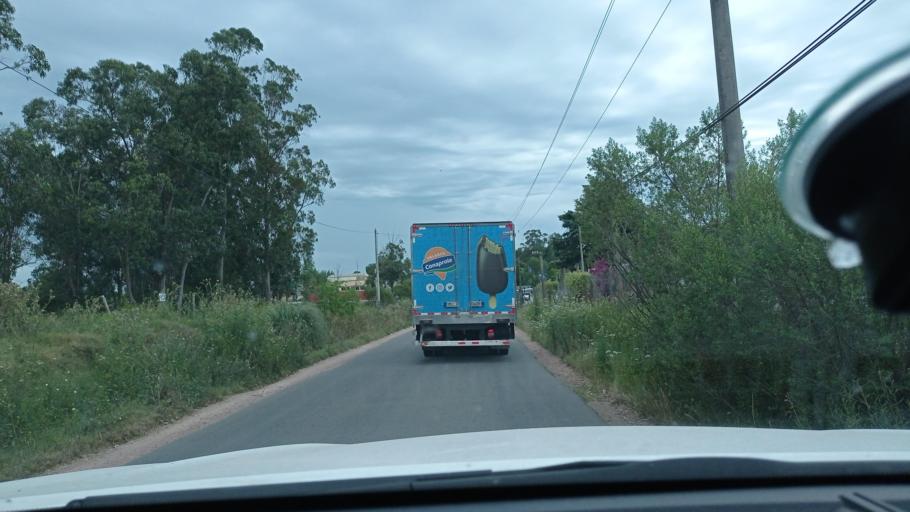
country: UY
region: Canelones
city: La Paz
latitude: -34.8078
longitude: -56.1894
